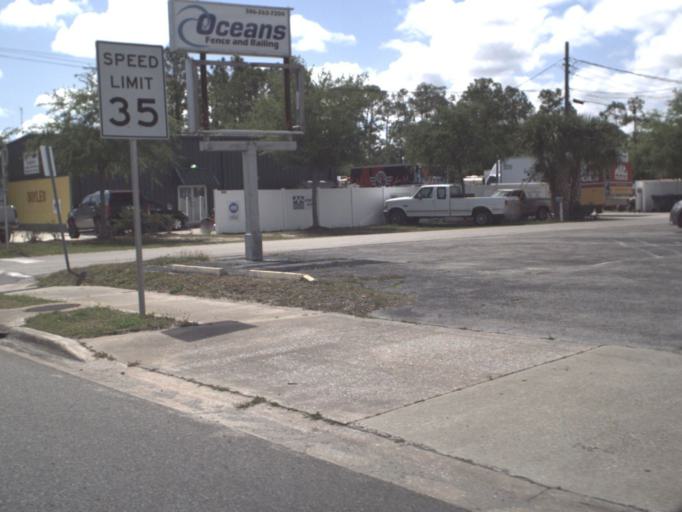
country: US
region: Florida
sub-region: Flagler County
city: Bunnell
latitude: 29.4700
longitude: -81.2640
